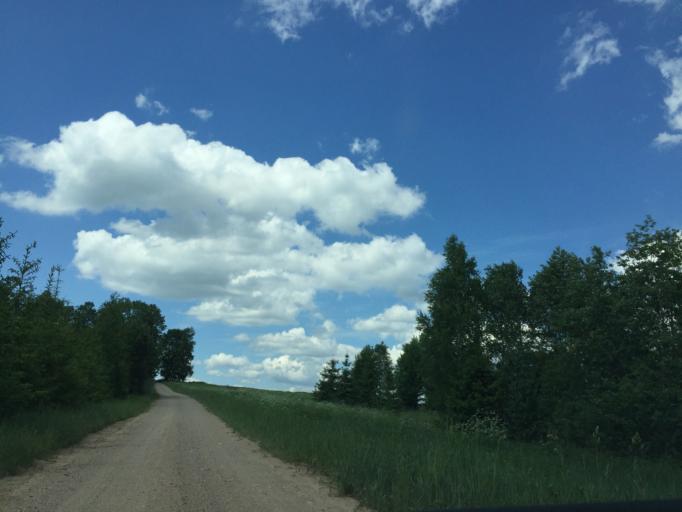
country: LV
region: Priekuli
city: Priekuli
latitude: 57.2338
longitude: 25.4241
